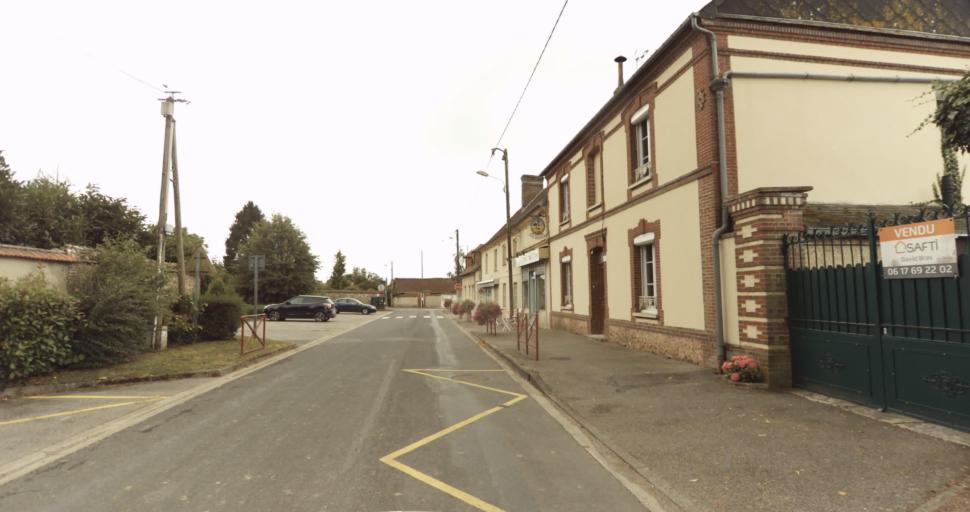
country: FR
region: Haute-Normandie
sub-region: Departement de l'Eure
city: Evreux
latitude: 48.9378
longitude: 1.1995
